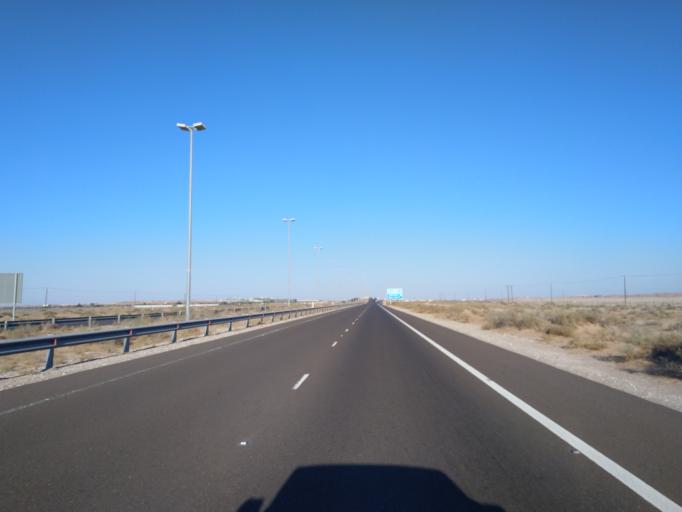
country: OM
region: Al Buraimi
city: Al Buraymi
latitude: 24.4996
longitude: 55.4398
